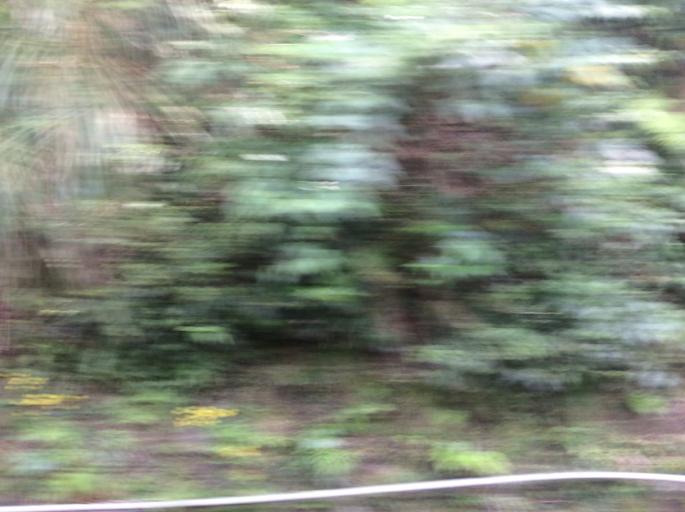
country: TW
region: Taipei
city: Taipei
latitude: 25.1658
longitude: 121.5433
